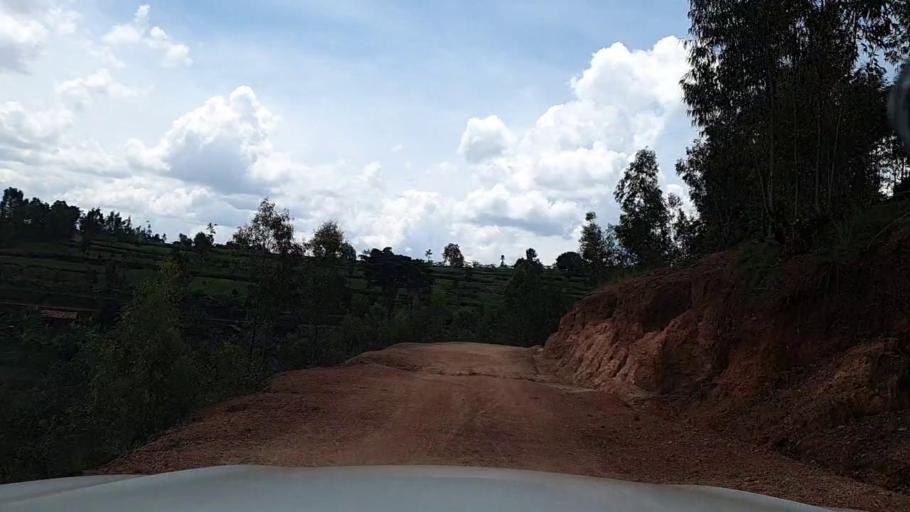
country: RW
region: Southern Province
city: Butare
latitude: -2.7557
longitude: 29.7486
